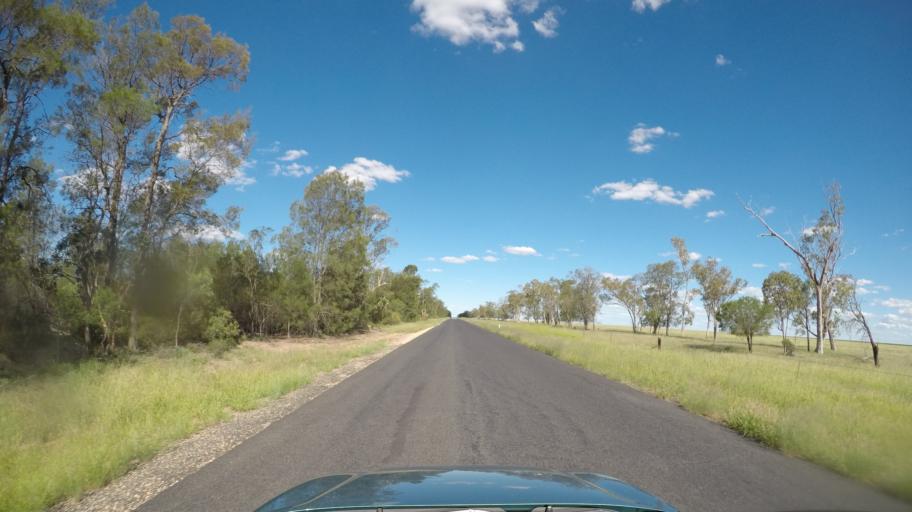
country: AU
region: Queensland
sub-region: Goondiwindi
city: Goondiwindi
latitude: -28.1498
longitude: 150.3252
